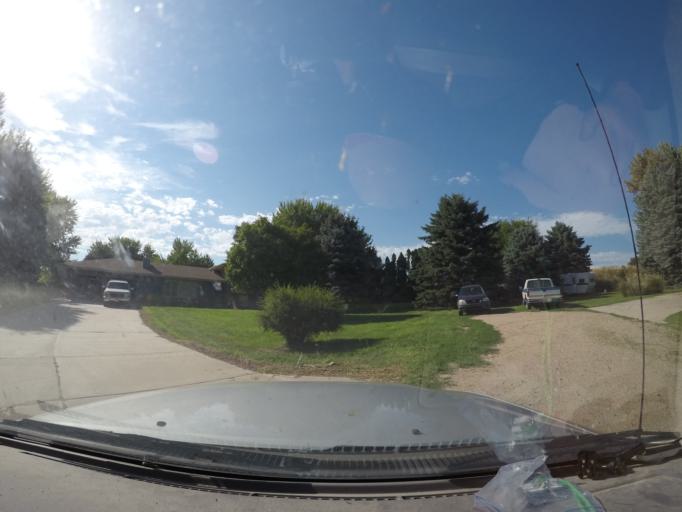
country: US
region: Nebraska
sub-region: Buffalo County
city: Kearney
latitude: 40.7002
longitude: -99.1685
